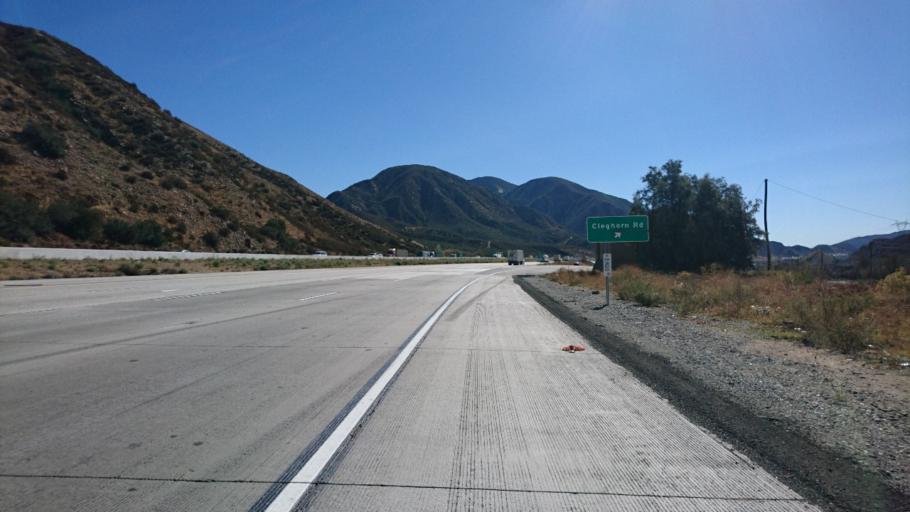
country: US
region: California
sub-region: San Bernardino County
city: Oak Hills
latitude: 34.3026
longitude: -117.4612
